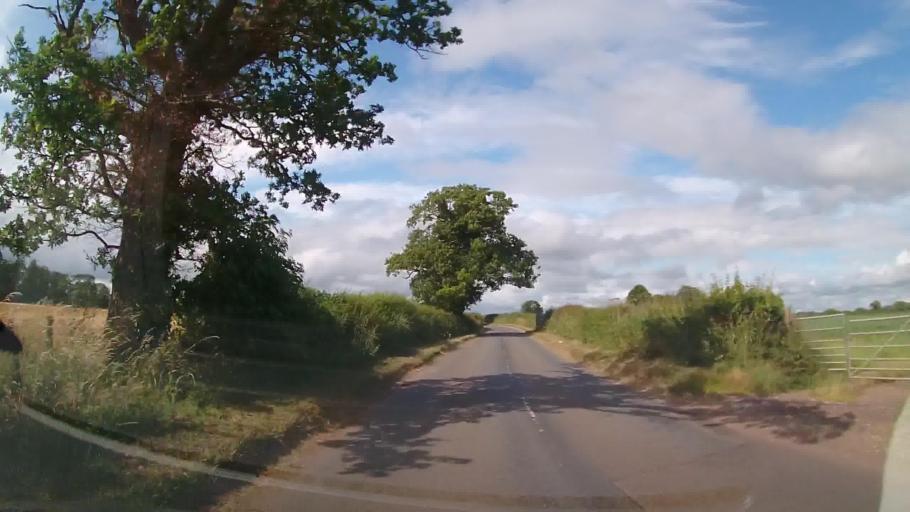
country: GB
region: England
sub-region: Shropshire
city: Petton
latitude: 52.8418
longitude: -2.8049
